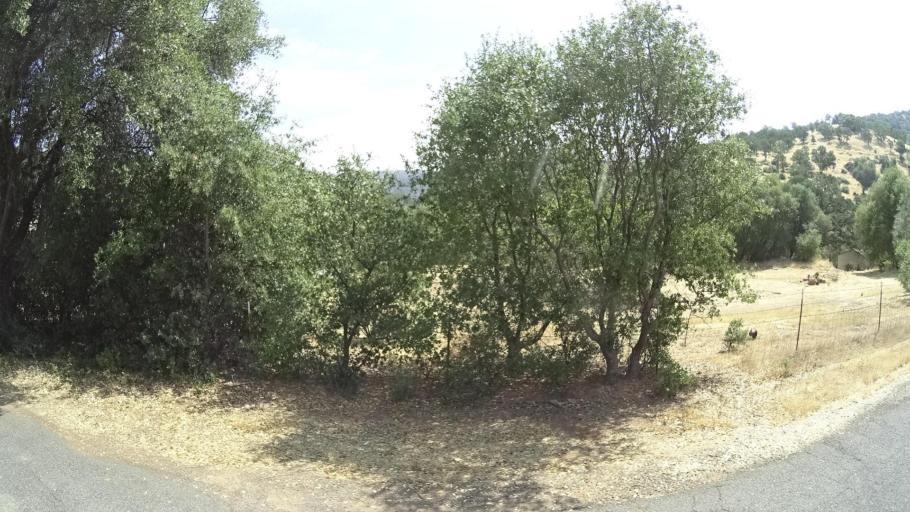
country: US
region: California
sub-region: Tuolumne County
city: Tuolumne City
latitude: 37.7155
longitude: -120.1939
